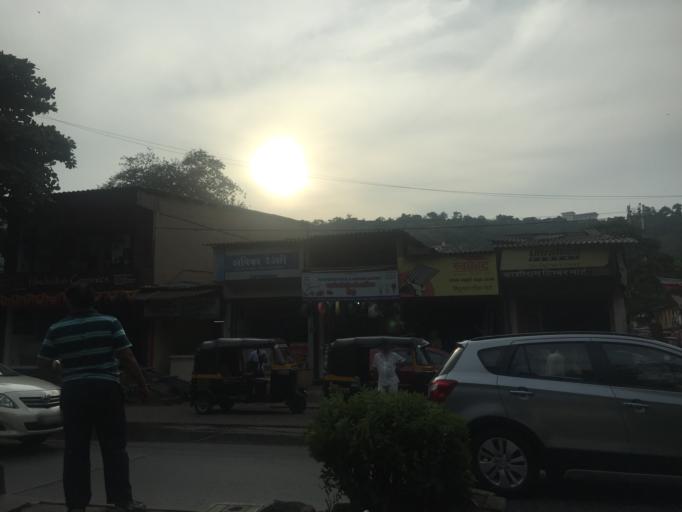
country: IN
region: Maharashtra
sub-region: Mumbai Suburban
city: Powai
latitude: 19.1216
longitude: 72.9255
